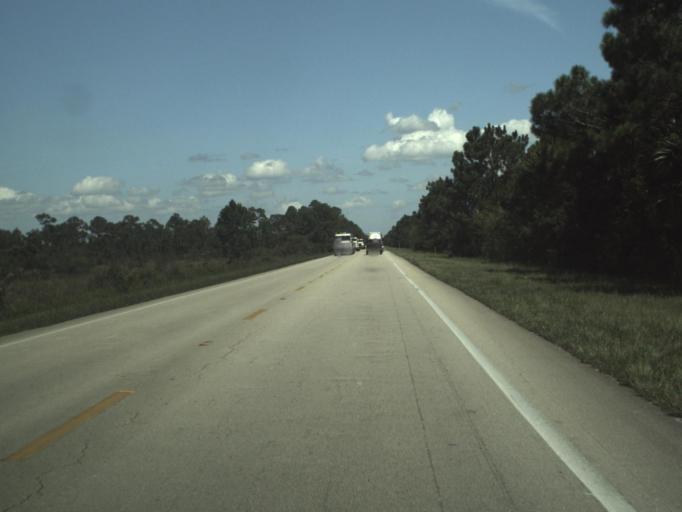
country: US
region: Florida
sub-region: Martin County
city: Indiantown
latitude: 26.9780
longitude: -80.4040
